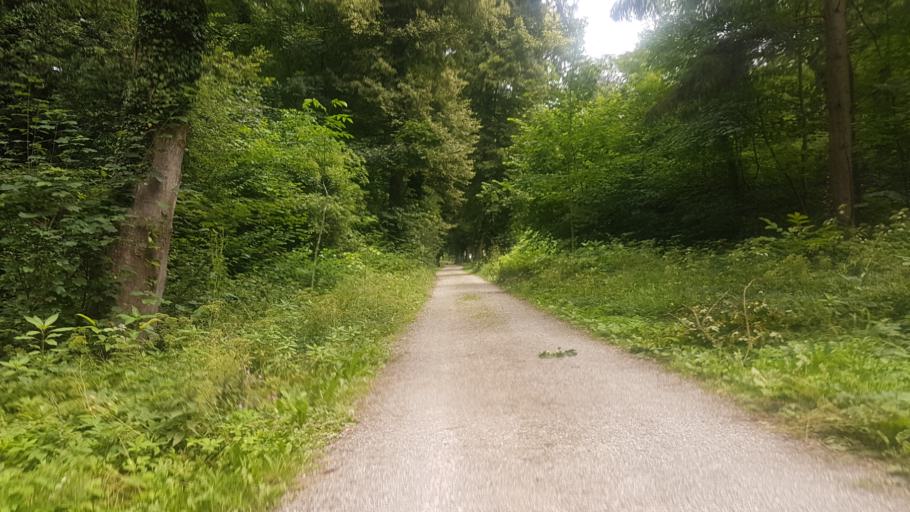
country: DE
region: Bavaria
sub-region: Swabia
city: Lauingen
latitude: 48.5635
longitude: 10.4281
